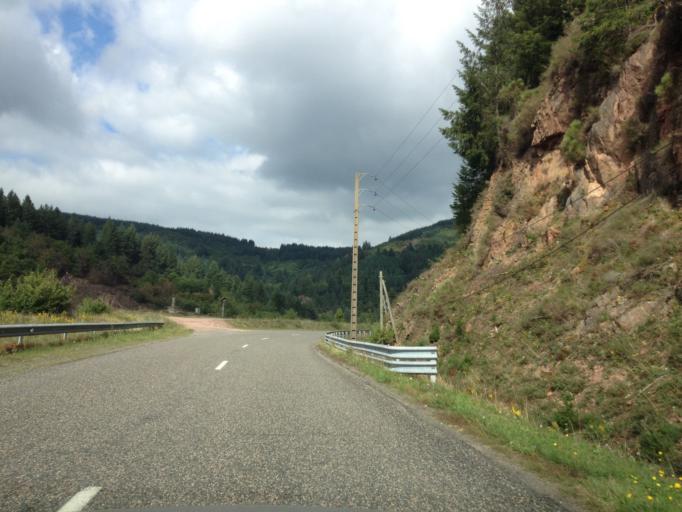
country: FR
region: Rhone-Alpes
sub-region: Departement de la Loire
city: Renaison
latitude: 46.0418
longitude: 3.8680
